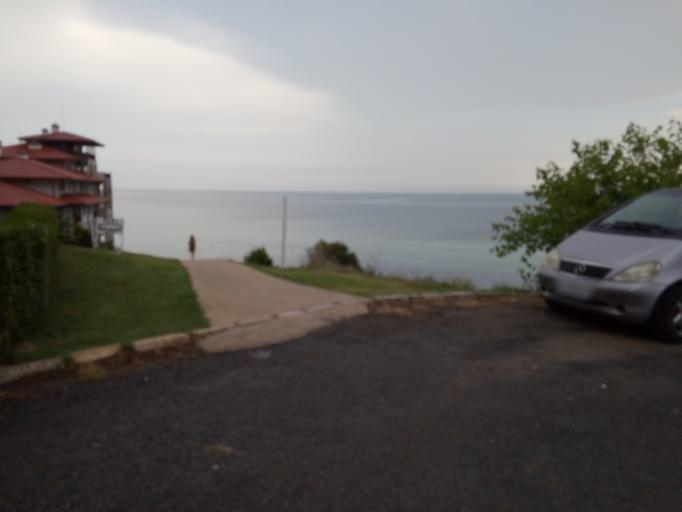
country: BG
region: Burgas
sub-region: Obshtina Nesebur
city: Sveti Vlas
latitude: 42.7058
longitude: 27.7754
